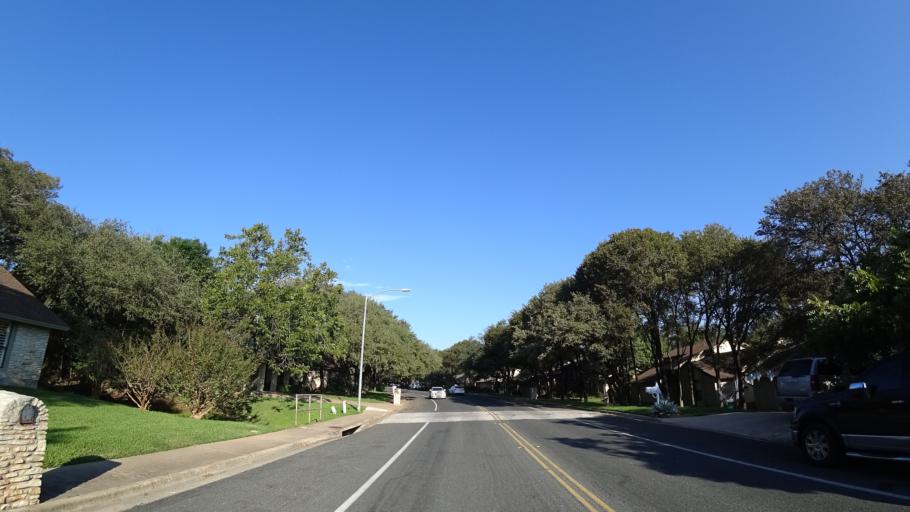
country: US
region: Texas
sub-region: Travis County
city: Rollingwood
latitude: 30.2655
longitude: -97.8040
